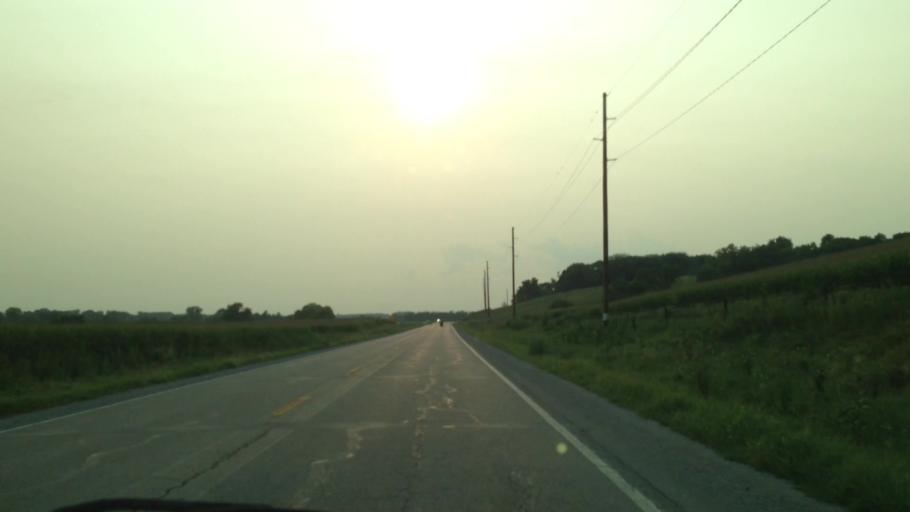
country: US
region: Iowa
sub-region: Benton County
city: Walford
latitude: 41.7978
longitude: -91.9219
